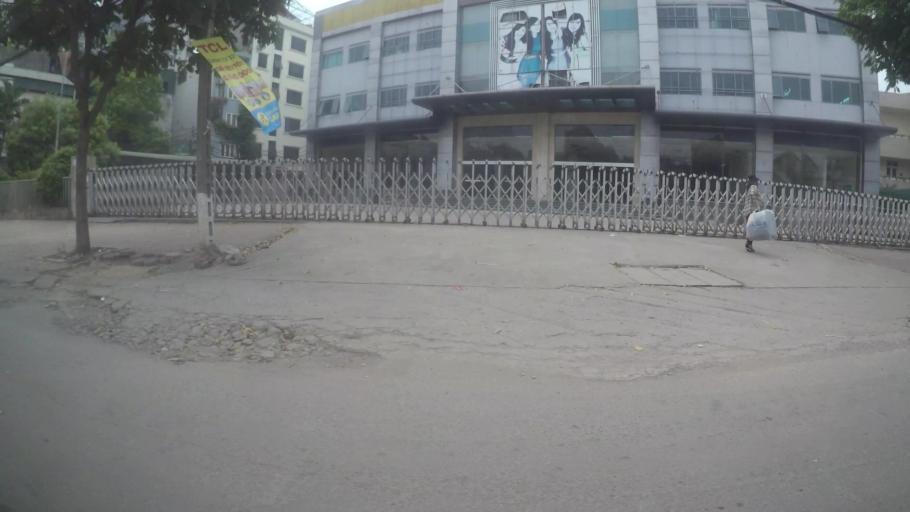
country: VN
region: Ha Noi
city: Ha Dong
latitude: 20.9783
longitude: 105.7741
